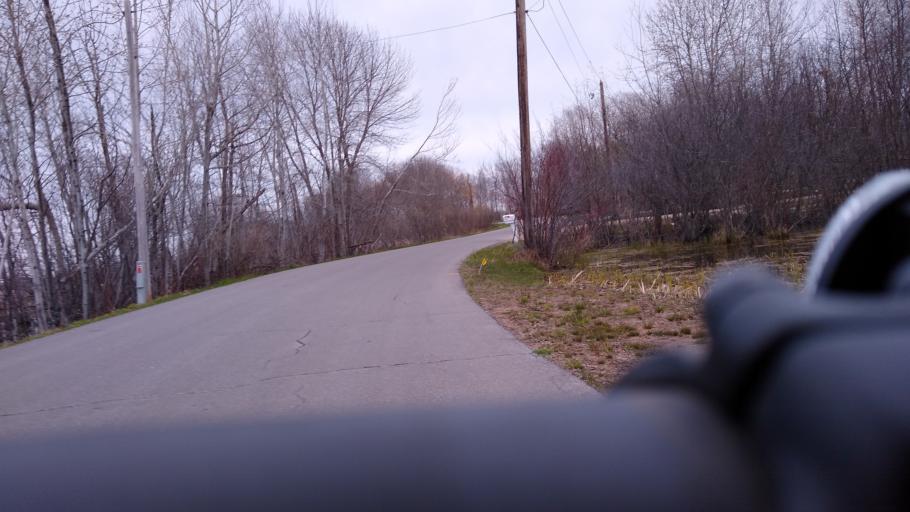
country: US
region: Michigan
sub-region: Delta County
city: Escanaba
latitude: 45.7049
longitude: -87.0843
